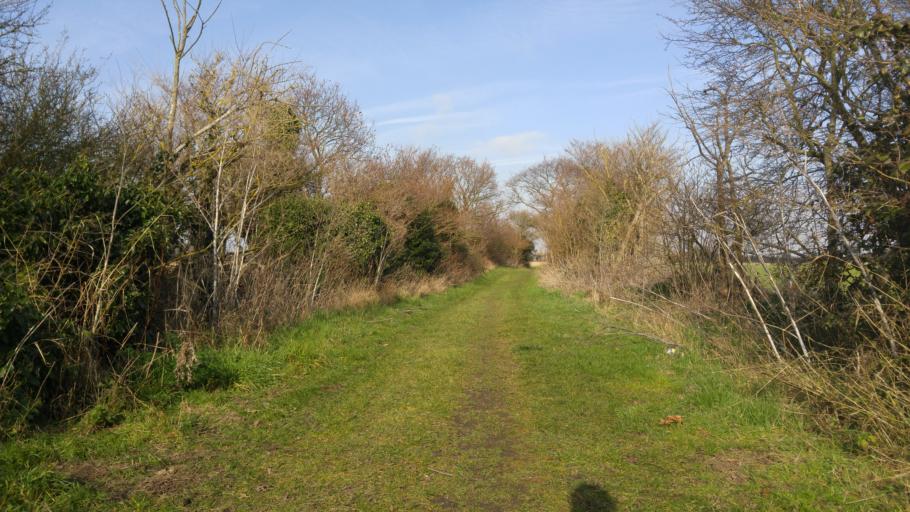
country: GB
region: England
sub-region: Essex
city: Little Clacton
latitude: 51.8213
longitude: 1.1706
